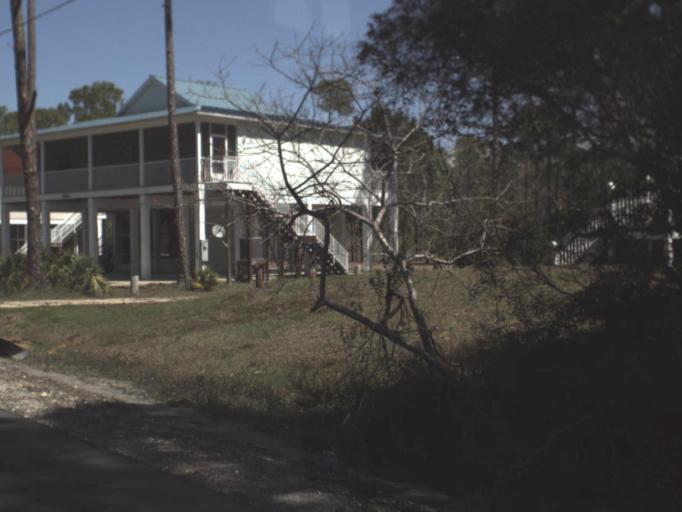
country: US
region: Florida
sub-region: Gulf County
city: Port Saint Joe
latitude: 29.7014
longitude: -85.3058
